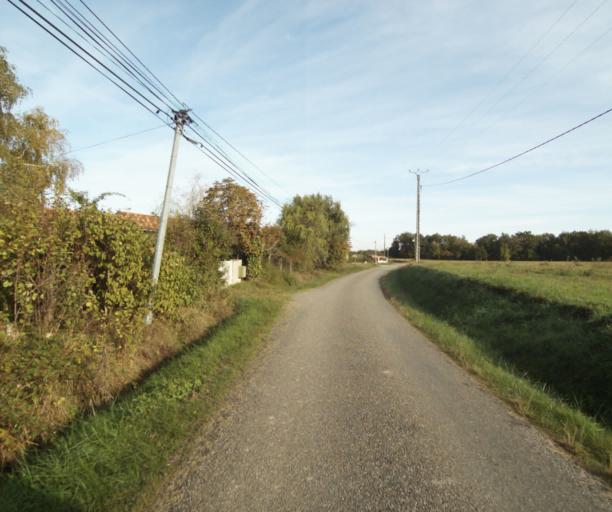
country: FR
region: Midi-Pyrenees
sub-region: Departement de la Haute-Garonne
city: Villemur-sur-Tarn
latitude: 43.9066
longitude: 1.5151
